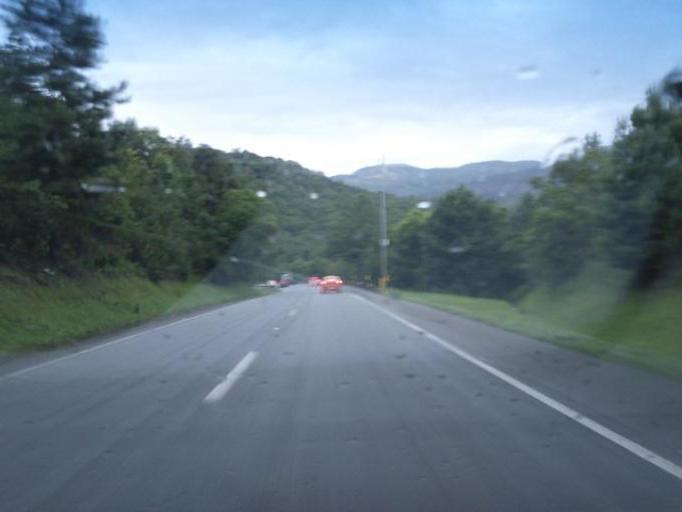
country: BR
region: Parana
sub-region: Sao Jose Dos Pinhais
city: Sao Jose dos Pinhais
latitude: -25.8545
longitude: -48.9984
